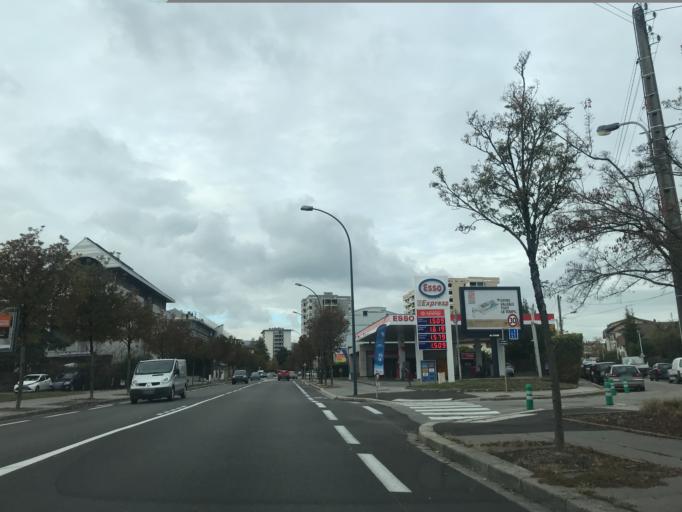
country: FR
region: Rhone-Alpes
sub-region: Departement de la Haute-Savoie
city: Annecy-le-Vieux
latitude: 45.9162
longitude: 6.1287
